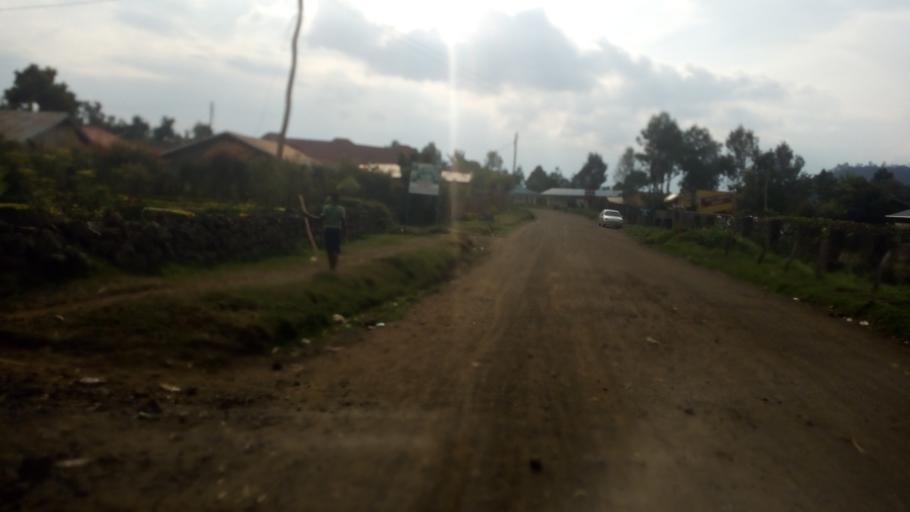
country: UG
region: Western Region
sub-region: Kisoro District
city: Kisoro
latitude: -1.2913
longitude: 29.6957
